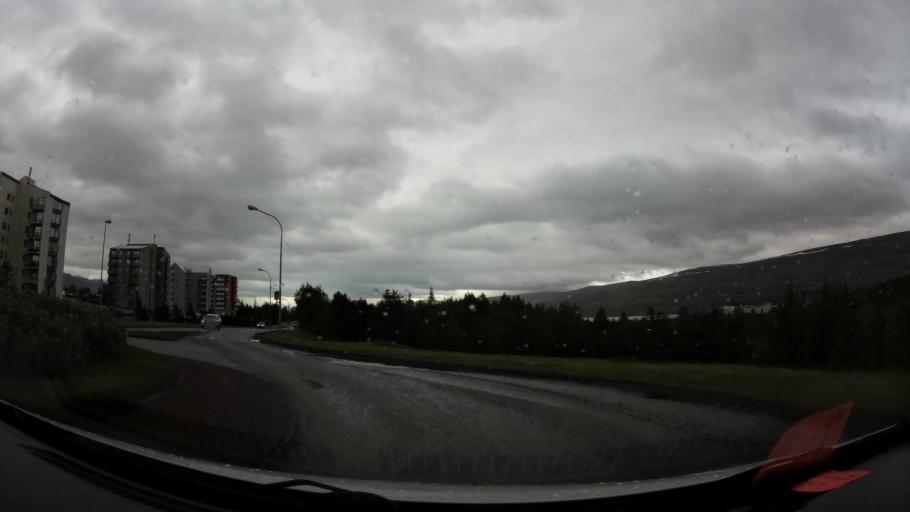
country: IS
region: Northeast
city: Akureyri
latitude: 65.6842
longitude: -18.1289
